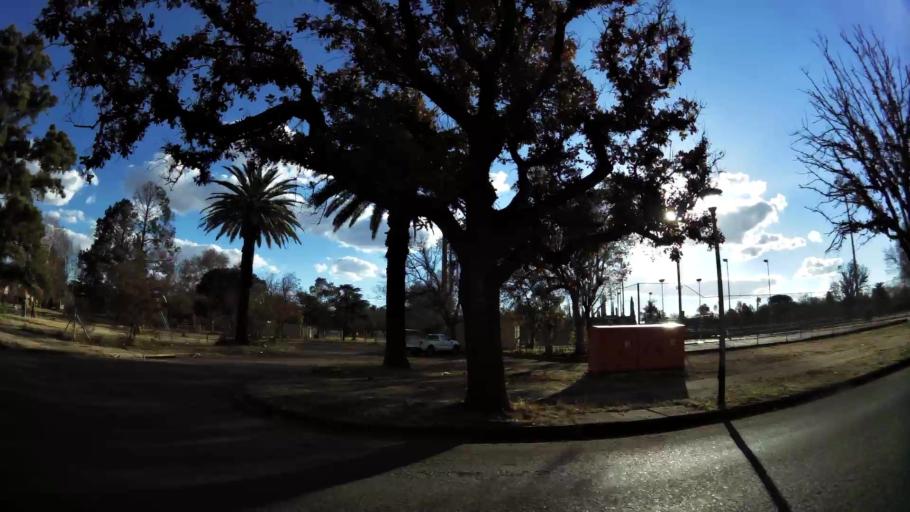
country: ZA
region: North-West
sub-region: Dr Kenneth Kaunda District Municipality
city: Potchefstroom
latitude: -26.7121
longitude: 27.0911
